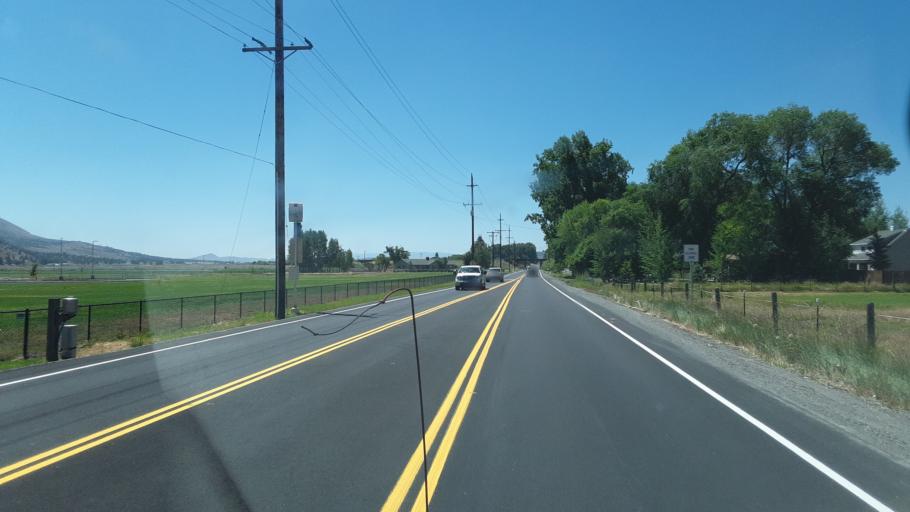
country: US
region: Oregon
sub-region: Klamath County
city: Altamont
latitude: 42.1506
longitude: -121.6983
